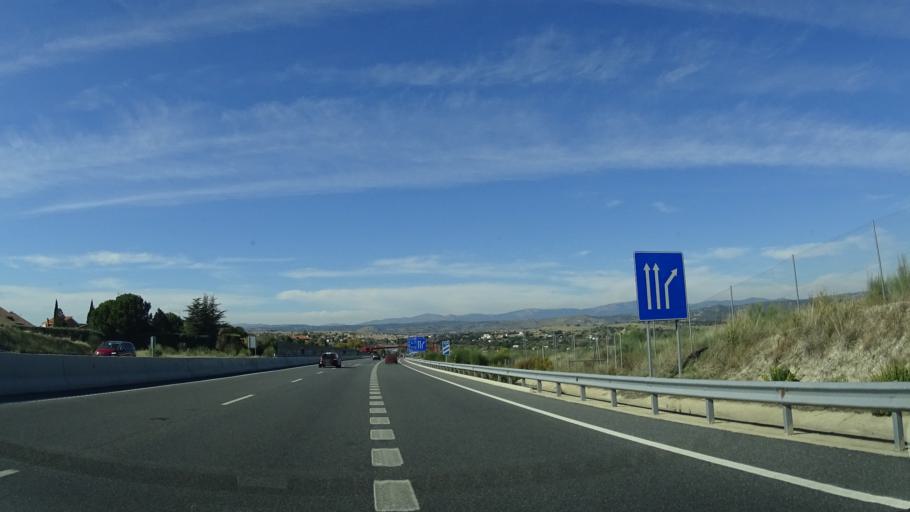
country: ES
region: Madrid
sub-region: Provincia de Madrid
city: Villanueva del Pardillo
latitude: 40.4830
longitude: -3.9273
